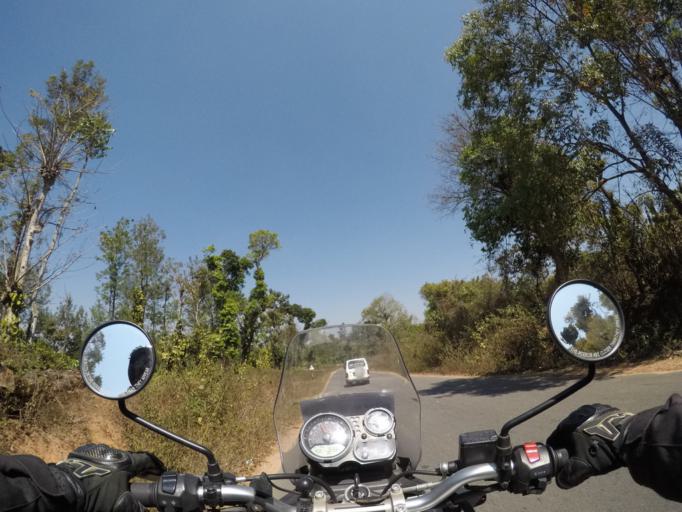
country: IN
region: Karnataka
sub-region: Chikmagalur
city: Mudigere
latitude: 13.0670
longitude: 75.6780
